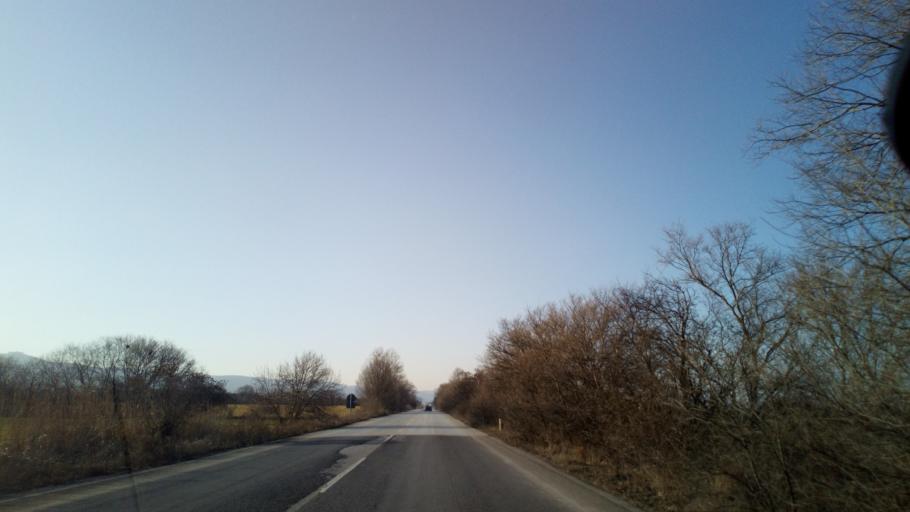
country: GR
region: Central Macedonia
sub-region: Nomos Thessalonikis
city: Agios Vasileios
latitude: 40.6599
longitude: 23.1254
